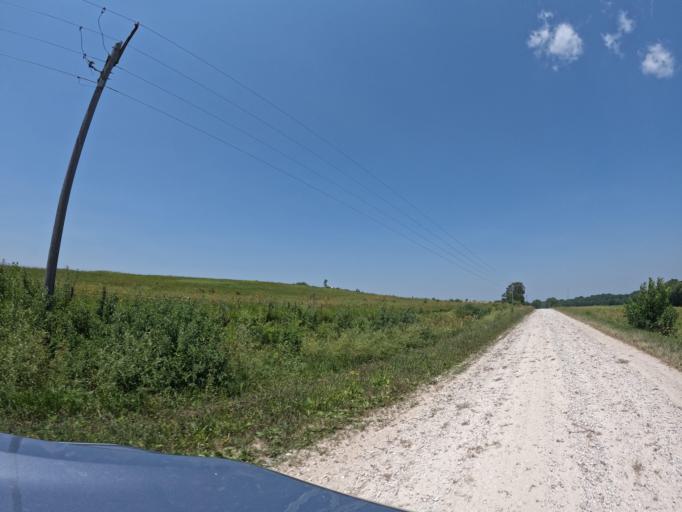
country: US
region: Iowa
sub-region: Keokuk County
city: Sigourney
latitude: 41.2967
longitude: -92.2095
